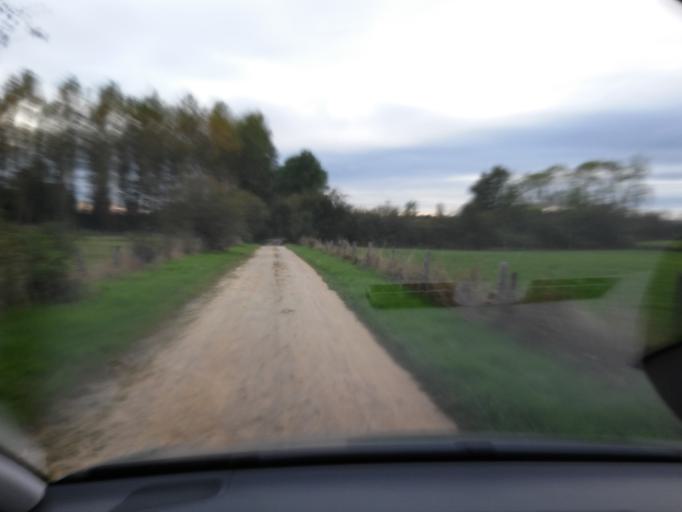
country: BE
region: Wallonia
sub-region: Province du Luxembourg
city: Habay-la-Vieille
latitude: 49.6808
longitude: 5.6607
